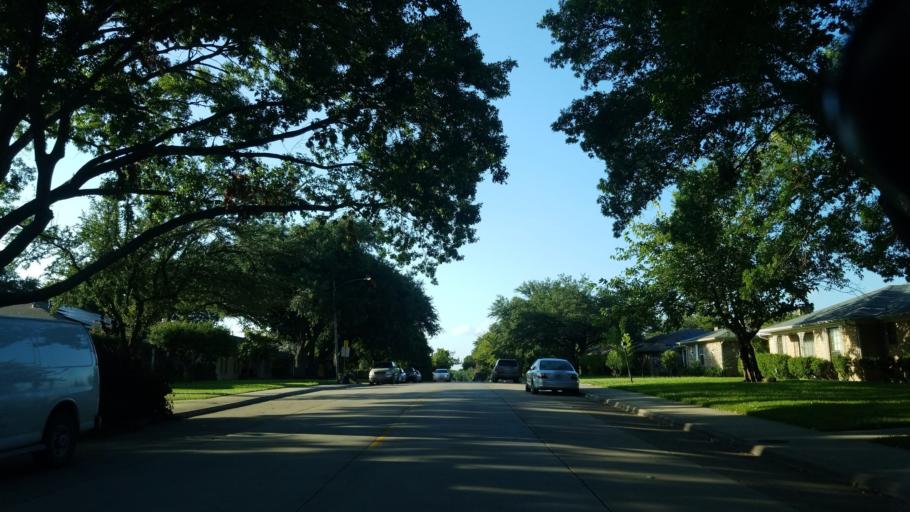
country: US
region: Texas
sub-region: Dallas County
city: Highland Park
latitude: 32.7880
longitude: -96.7123
